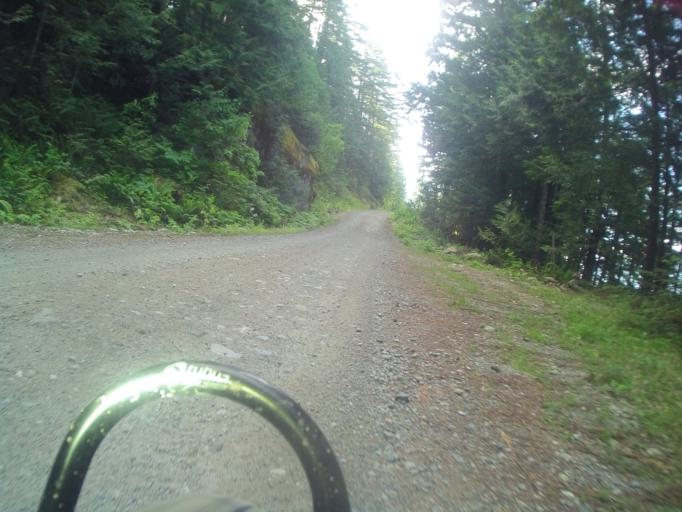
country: CA
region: British Columbia
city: Agassiz
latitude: 49.6671
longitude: -122.0083
